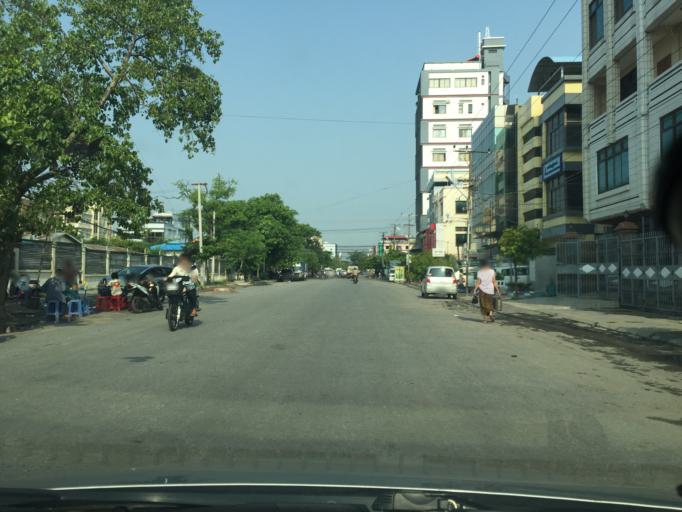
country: MM
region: Mandalay
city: Mandalay
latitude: 21.9709
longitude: 96.0832
